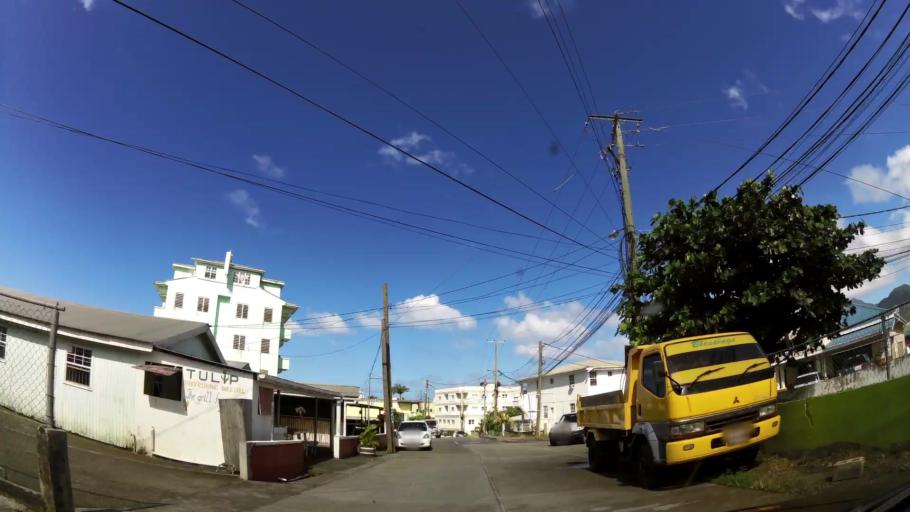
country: DM
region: Saint John
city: Portsmouth
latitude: 15.5551
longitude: -61.4578
